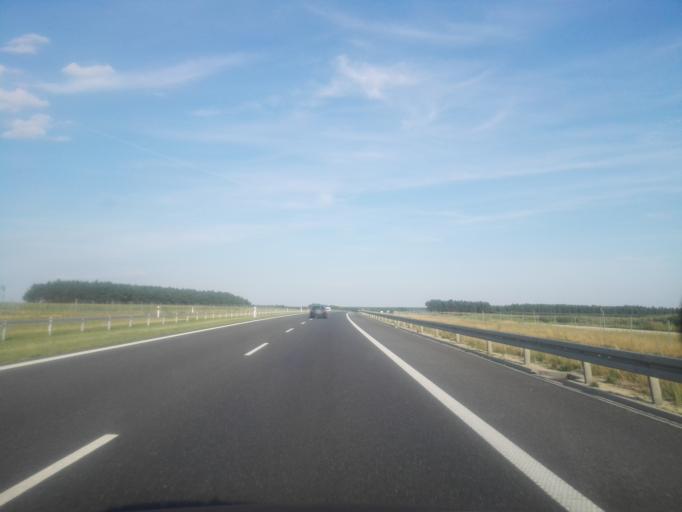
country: PL
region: Lodz Voivodeship
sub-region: Powiat wieruszowski
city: Wieruszow
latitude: 51.3367
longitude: 18.1310
